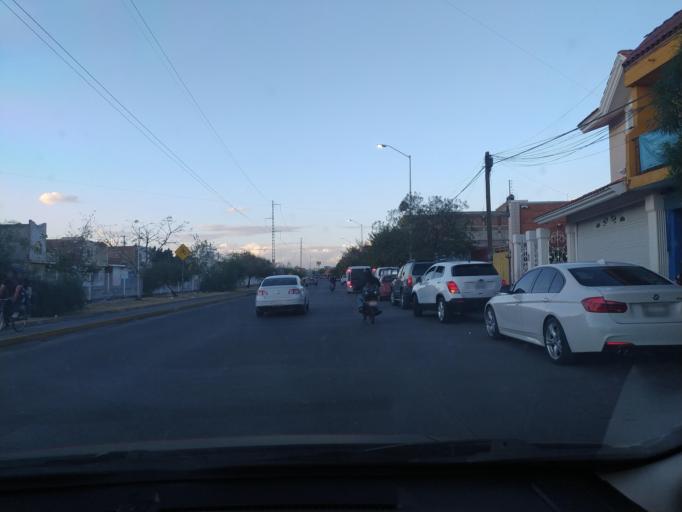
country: LA
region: Oudomxai
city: Muang La
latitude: 21.0249
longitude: 101.8694
